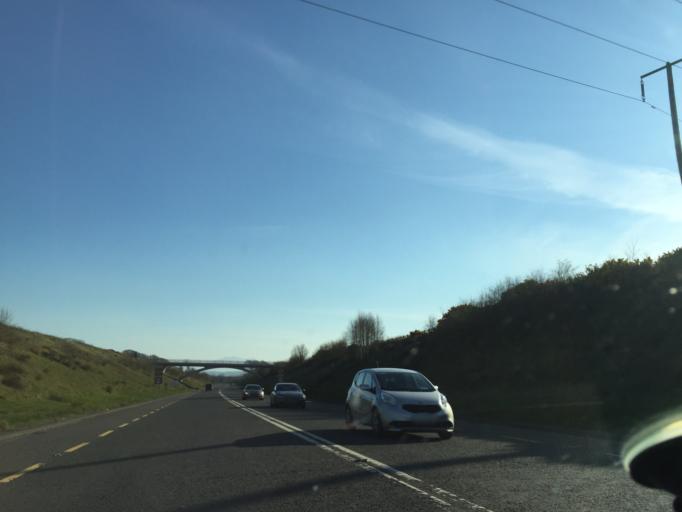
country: IE
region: Munster
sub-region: Ciarrai
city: Castleisland
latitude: 52.2064
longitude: -9.5677
